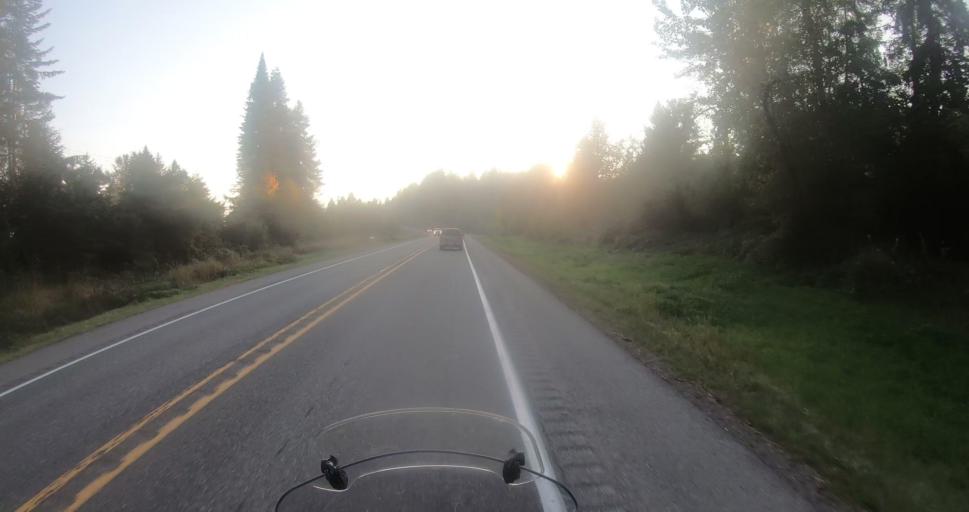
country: US
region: Washington
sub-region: Lewis County
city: Morton
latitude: 46.5134
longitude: -122.1728
